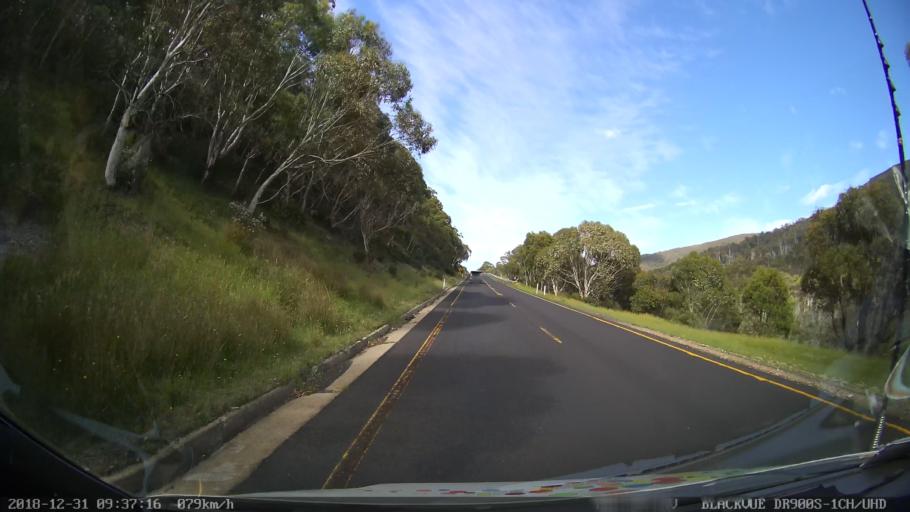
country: AU
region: New South Wales
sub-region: Snowy River
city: Jindabyne
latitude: -36.4651
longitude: 148.3777
